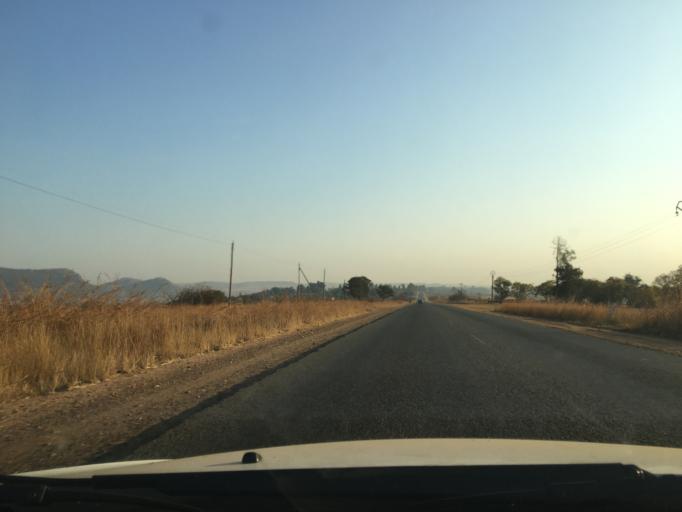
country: ZA
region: Gauteng
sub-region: West Rand District Municipality
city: Muldersdriseloop
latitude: -26.0105
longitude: 27.8585
